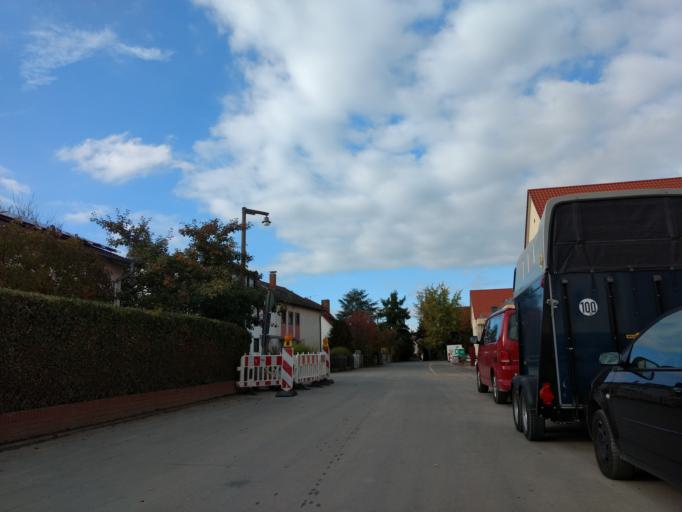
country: DE
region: Bavaria
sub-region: Regierungsbezirk Mittelfranken
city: Erlangen
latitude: 49.5903
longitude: 10.9592
